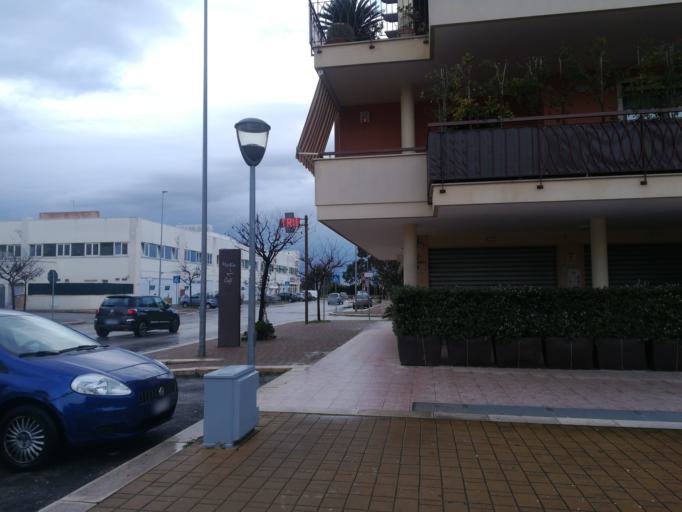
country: IT
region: Apulia
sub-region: Provincia di Bari
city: Polignano a Mare
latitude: 40.9935
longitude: 17.2122
